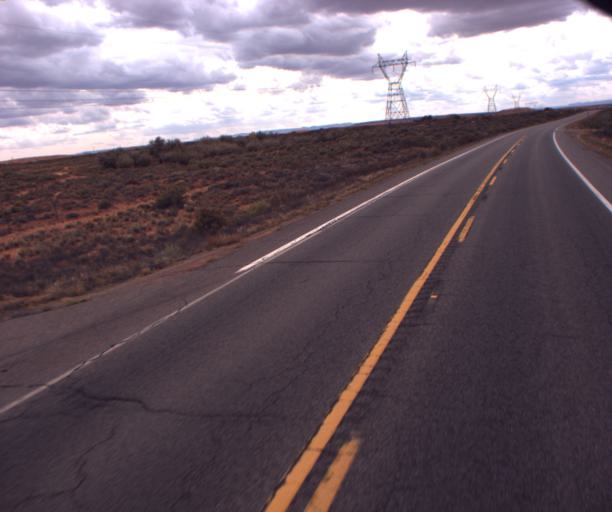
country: US
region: Arizona
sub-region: Navajo County
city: Kayenta
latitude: 36.8480
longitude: -109.8342
